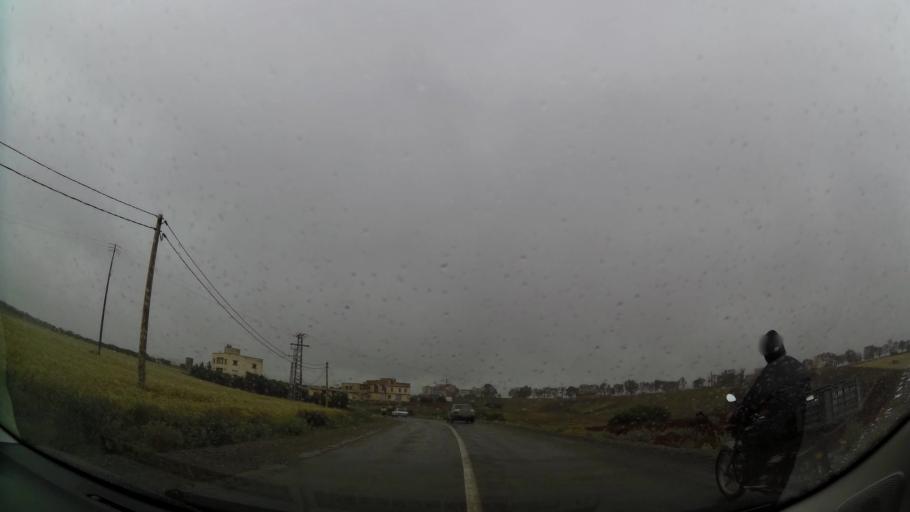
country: MA
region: Oriental
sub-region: Nador
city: Boudinar
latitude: 35.1333
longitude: -3.6254
